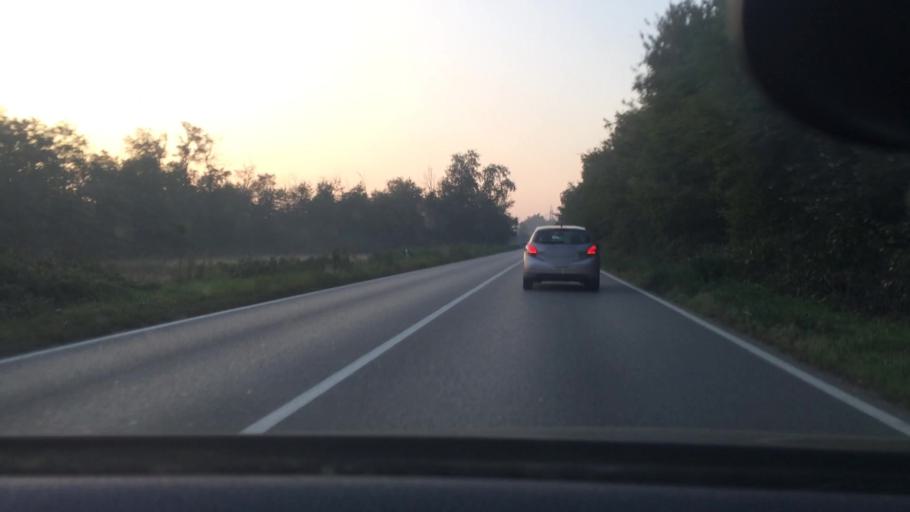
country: IT
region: Lombardy
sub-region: Citta metropolitana di Milano
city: Nerviano
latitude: 45.5344
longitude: 8.9670
